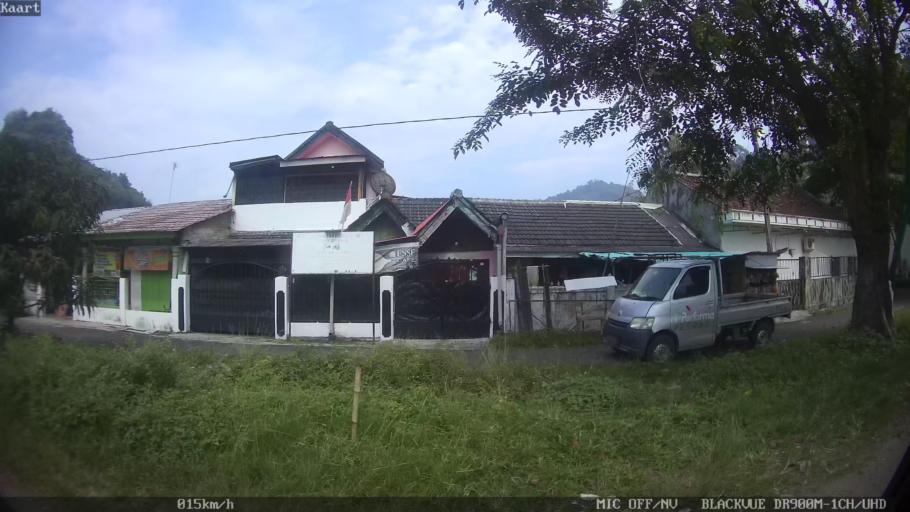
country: ID
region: Lampung
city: Bandarlampung
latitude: -5.4620
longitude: 105.2433
